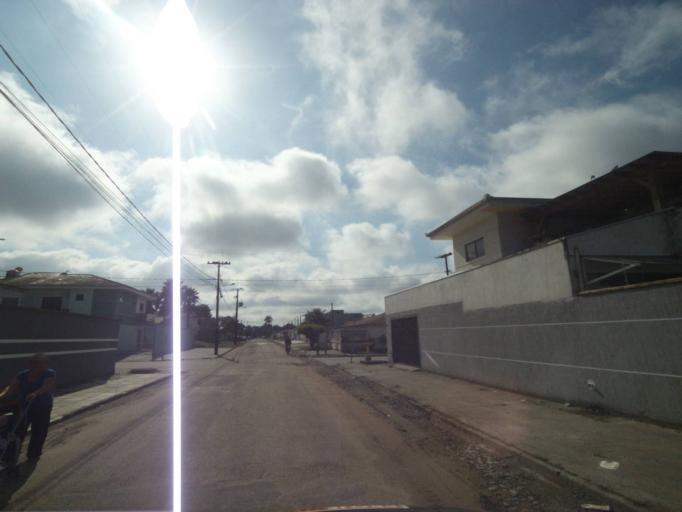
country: BR
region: Parana
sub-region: Paranagua
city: Paranagua
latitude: -25.5567
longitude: -48.5547
